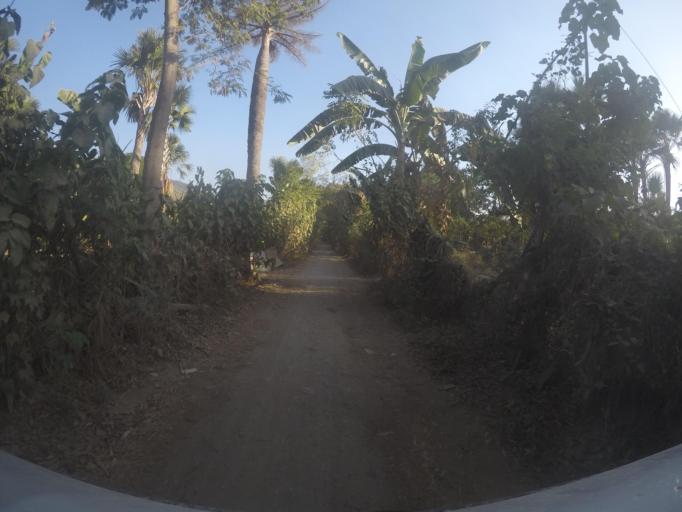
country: ID
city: Metinaro
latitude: -8.5464
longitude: 125.6667
